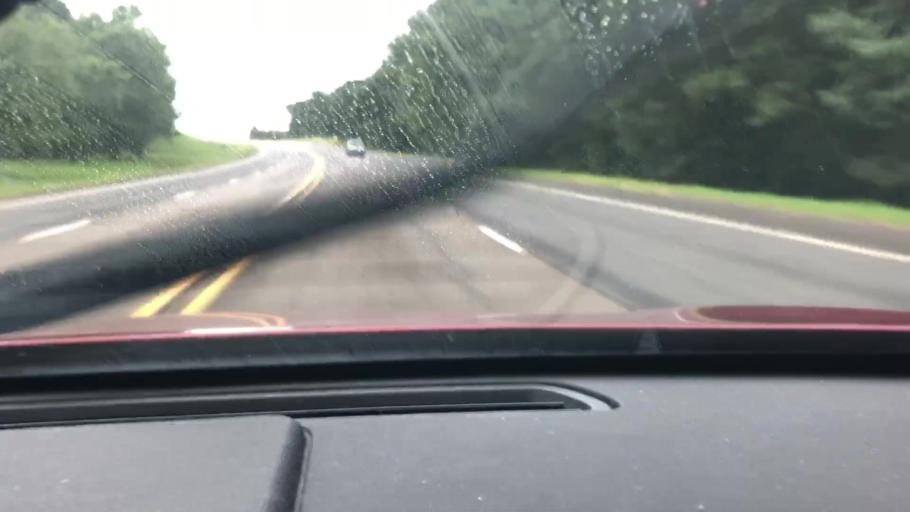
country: US
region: Arkansas
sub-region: Lafayette County
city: Lewisville
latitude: 33.3559
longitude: -93.5637
